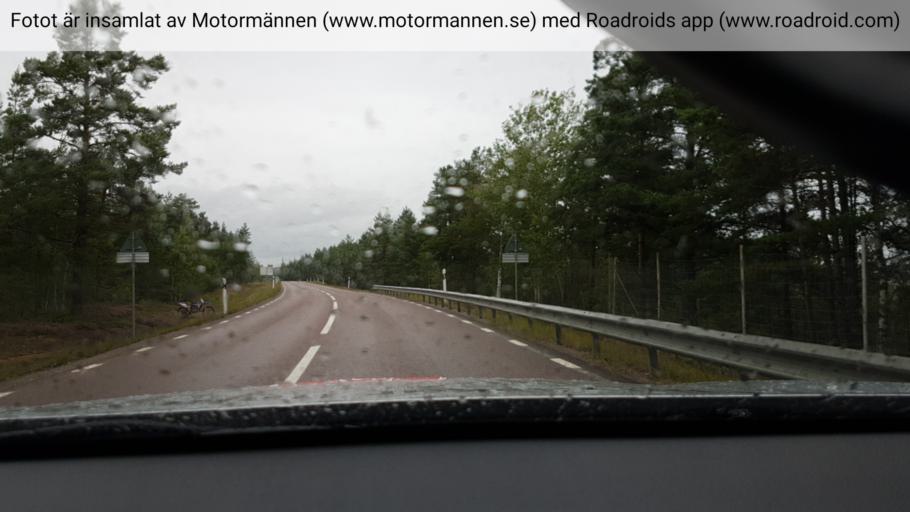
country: SE
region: Gaevleborg
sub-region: Gavle Kommun
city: Valbo
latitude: 60.5976
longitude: 16.9755
